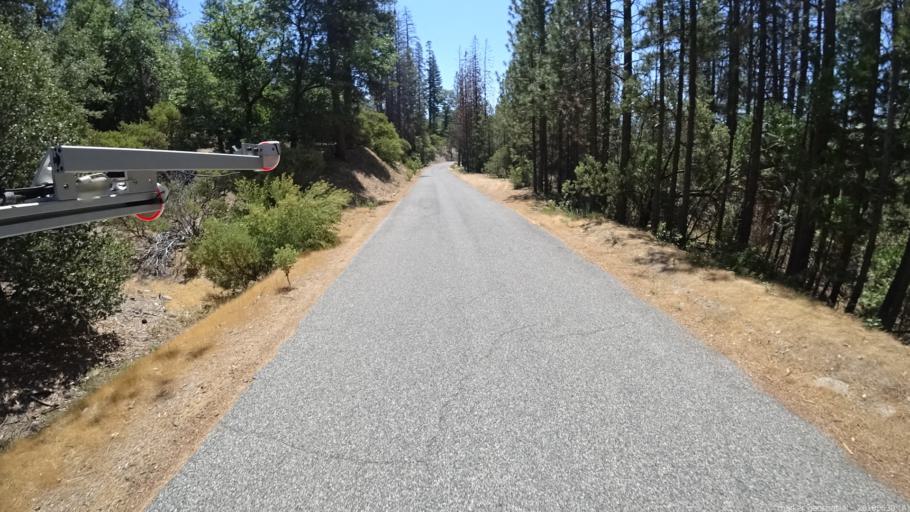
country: US
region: California
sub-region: Madera County
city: Oakhurst
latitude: 37.3602
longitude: -119.3480
